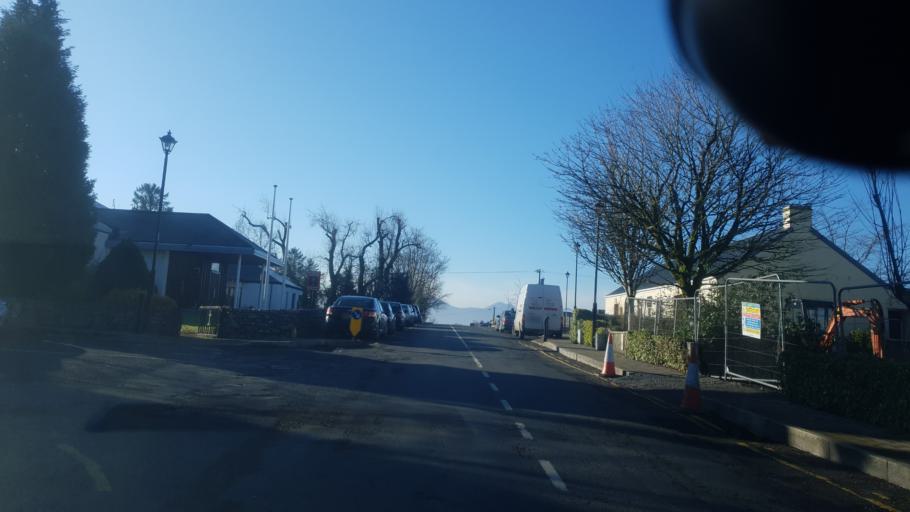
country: IE
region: Munster
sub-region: Ciarrai
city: Cill Airne
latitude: 52.0973
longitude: -9.4710
